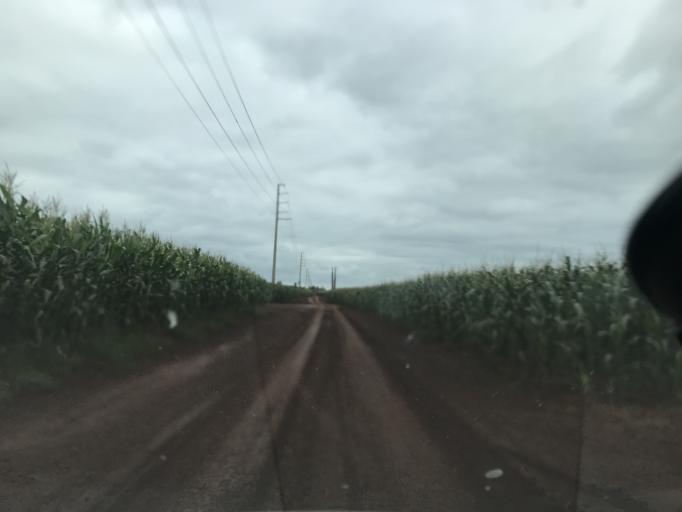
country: BR
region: Parana
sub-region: Palotina
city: Palotina
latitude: -24.3049
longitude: -53.8217
